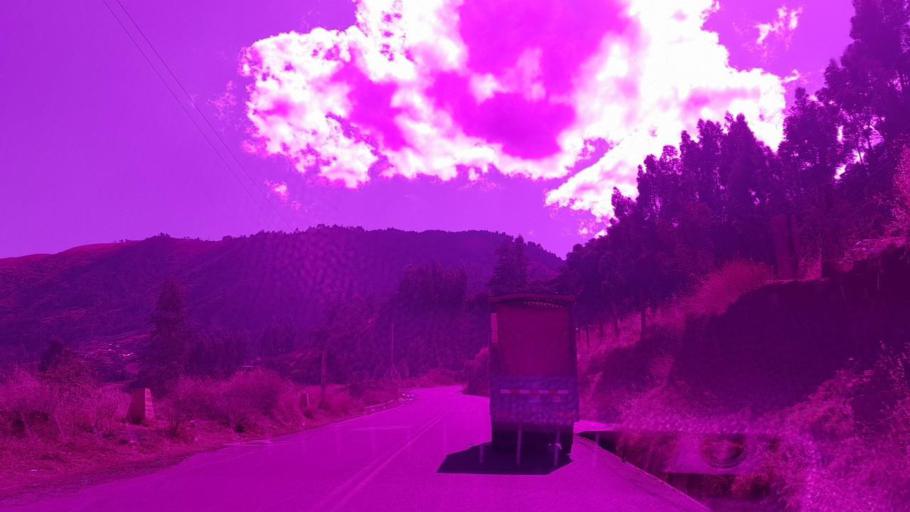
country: PE
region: Cusco
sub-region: Provincia de Cusco
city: Cusco
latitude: -13.5236
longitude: -71.9091
